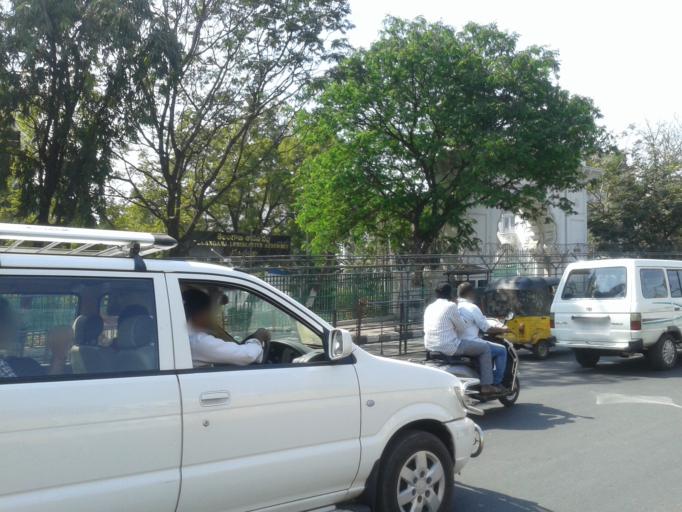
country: IN
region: Telangana
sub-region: Hyderabad
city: Hyderabad
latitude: 17.4022
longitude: 78.4684
